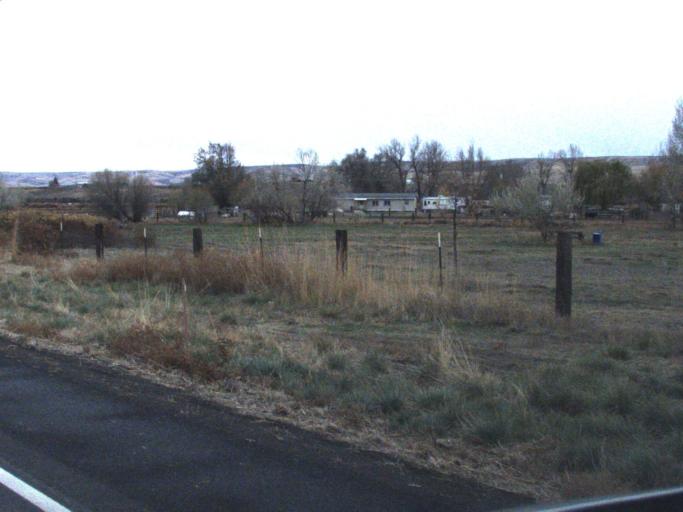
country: US
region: Washington
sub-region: Walla Walla County
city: Garrett
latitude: 46.0440
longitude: -118.6922
